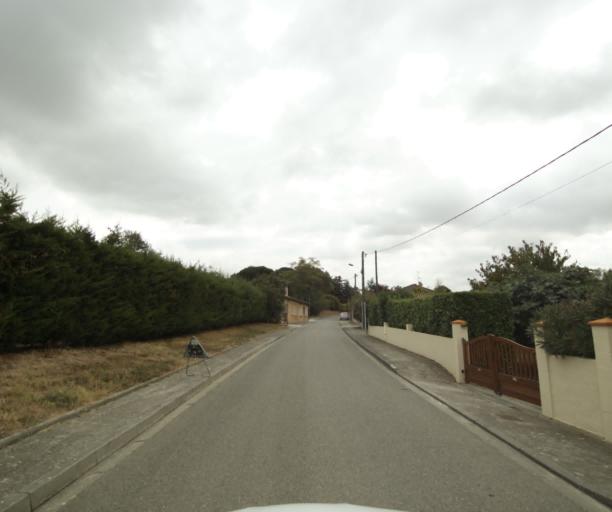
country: FR
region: Midi-Pyrenees
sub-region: Departement de la Haute-Garonne
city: Villefranche-de-Lauragais
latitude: 43.4077
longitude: 1.7129
